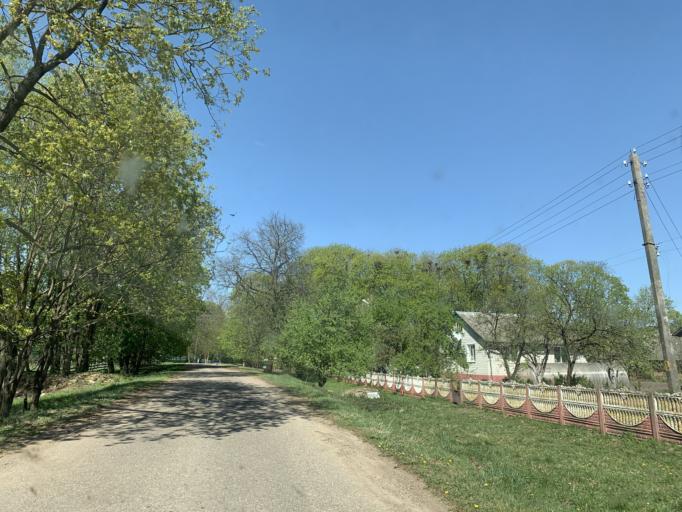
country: BY
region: Minsk
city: Kapyl'
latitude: 53.2582
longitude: 26.9529
